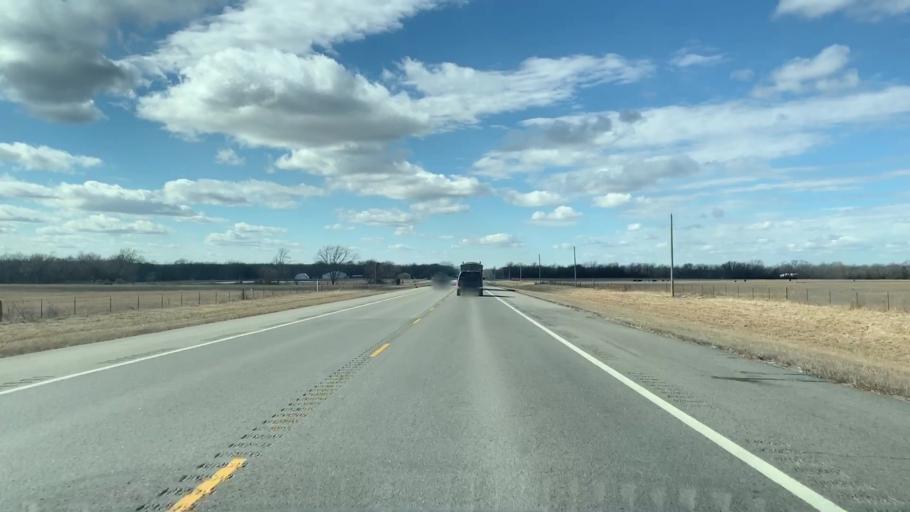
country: US
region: Kansas
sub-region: Cherokee County
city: Columbus
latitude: 37.3400
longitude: -94.9145
